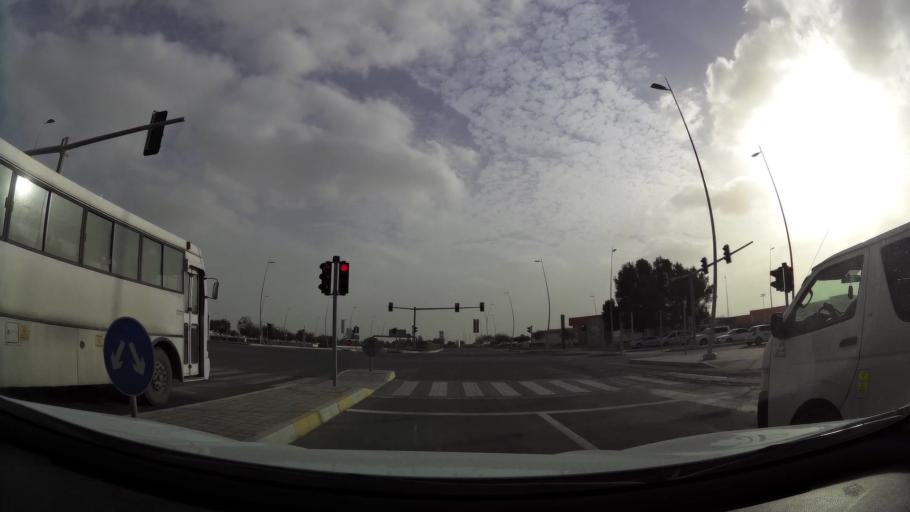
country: AE
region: Abu Dhabi
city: Abu Dhabi
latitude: 24.4962
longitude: 54.5913
